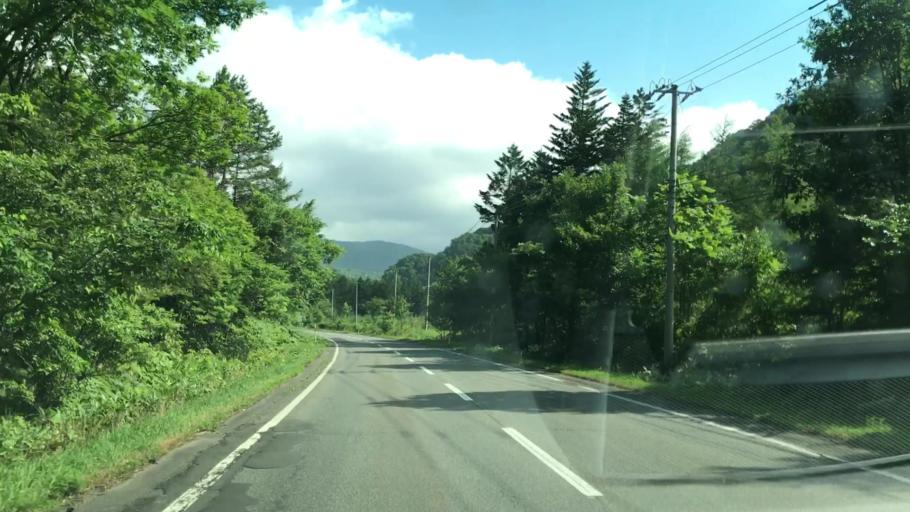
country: JP
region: Hokkaido
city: Shizunai-furukawacho
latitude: 42.8258
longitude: 142.4165
